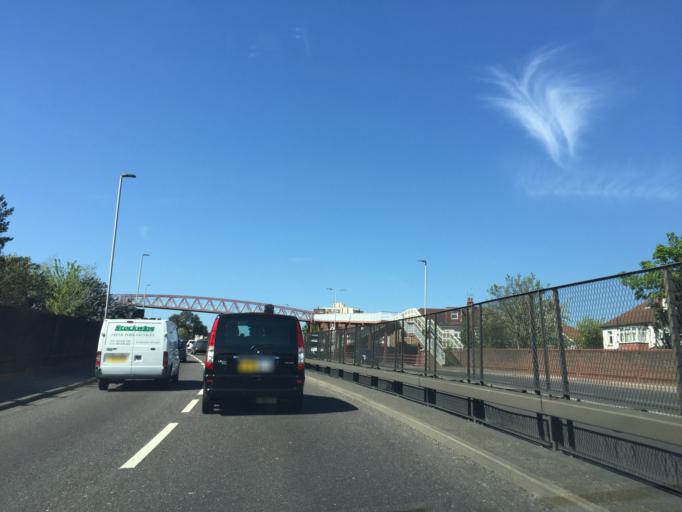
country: GB
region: England
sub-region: Greater London
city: Woodford Green
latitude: 51.5773
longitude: 0.0353
